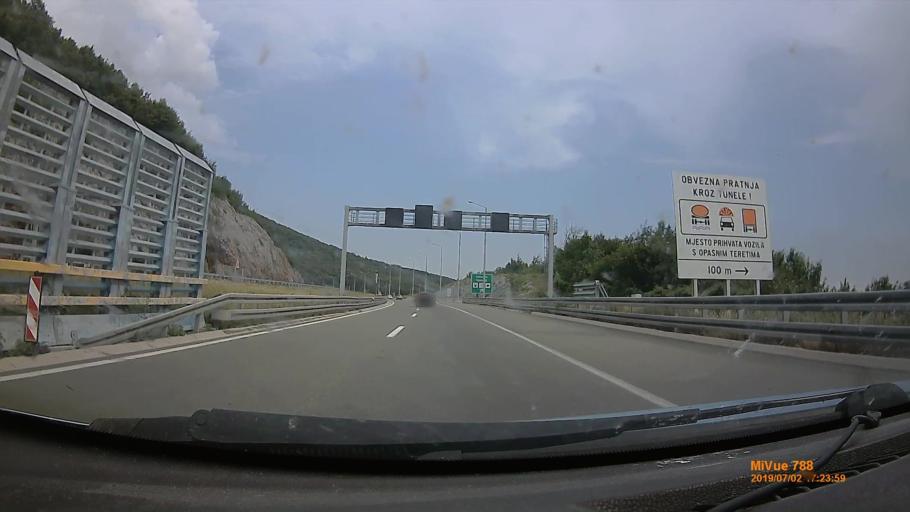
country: HR
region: Primorsko-Goranska
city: Hreljin
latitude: 45.3258
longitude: 14.6204
